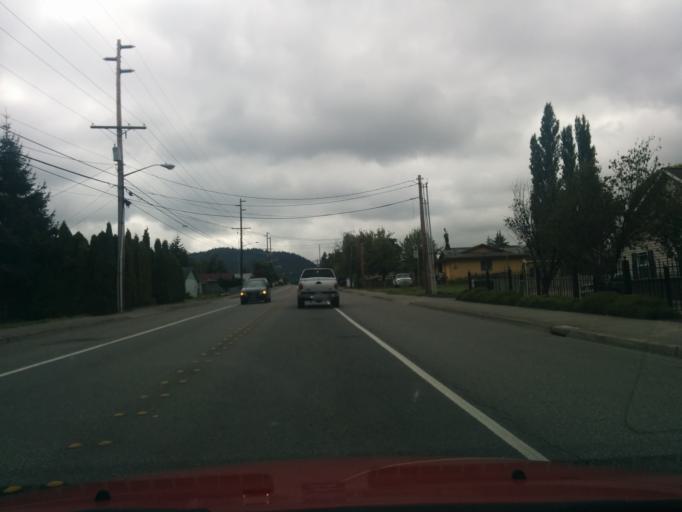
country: US
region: Washington
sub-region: Skagit County
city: Mount Vernon
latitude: 48.4237
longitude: -122.3135
